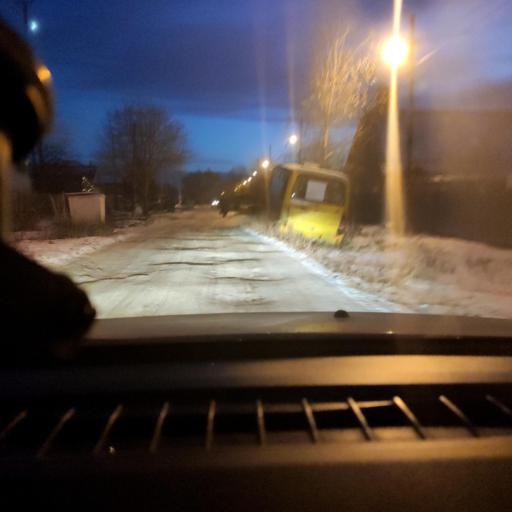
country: RU
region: Samara
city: Petra-Dubrava
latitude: 53.2566
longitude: 50.3341
